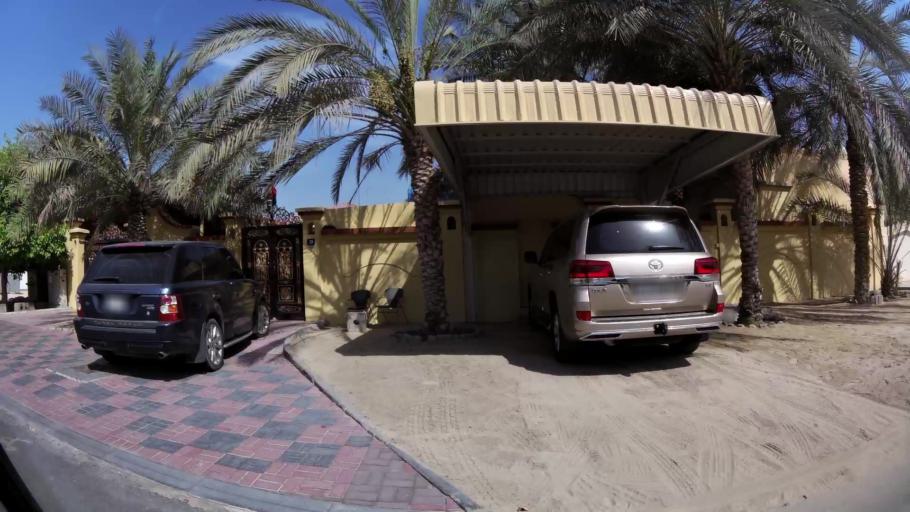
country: AE
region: Ash Shariqah
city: Sharjah
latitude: 25.2709
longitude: 55.4111
